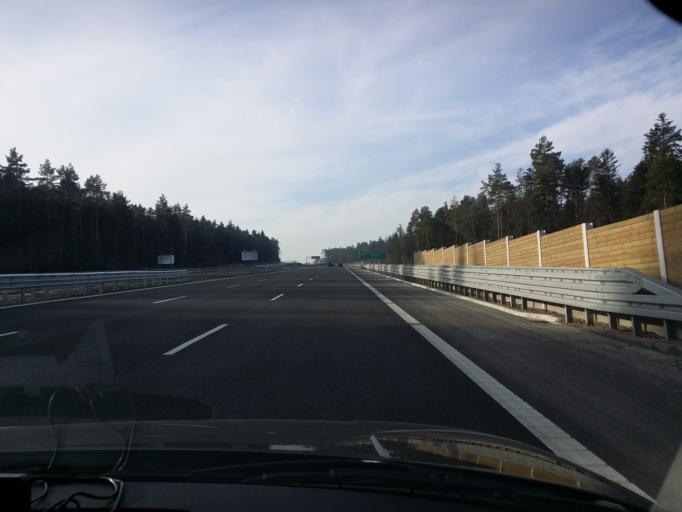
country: PL
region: Swietokrzyskie
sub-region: Powiat skarzyski
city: Skarzysko-Kamienna
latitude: 51.1519
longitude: 20.8437
